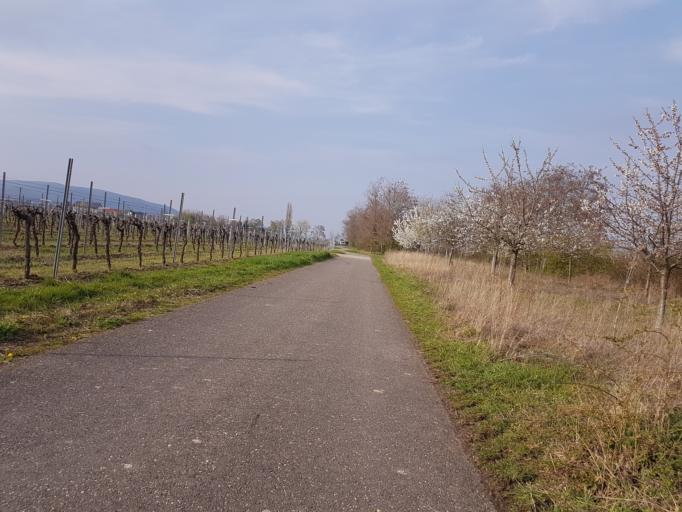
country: DE
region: Rheinland-Pfalz
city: Edesheim
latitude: 49.2749
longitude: 8.1381
